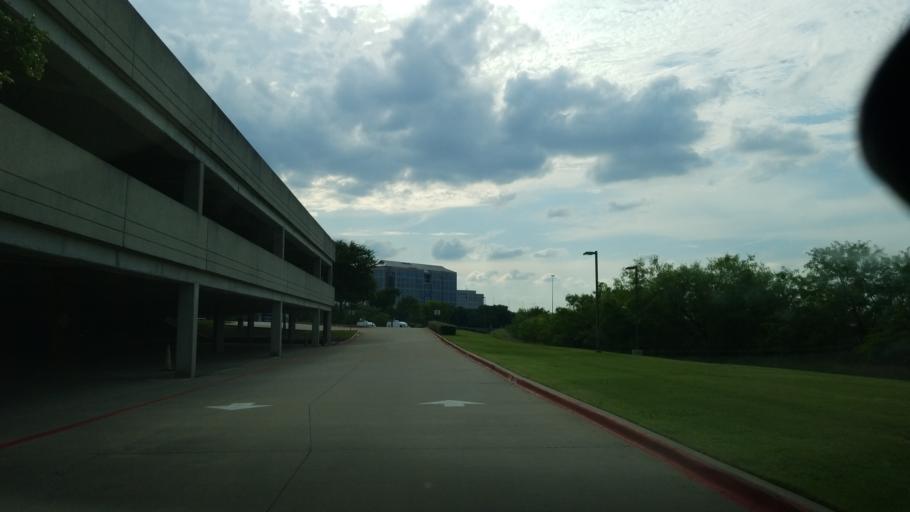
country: US
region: Texas
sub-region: Dallas County
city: Farmers Branch
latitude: 32.8944
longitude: -96.9634
